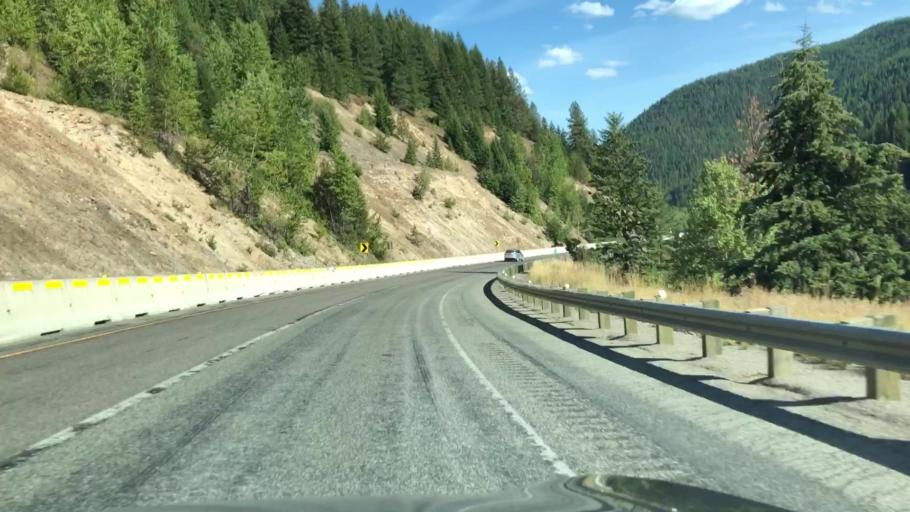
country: US
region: Montana
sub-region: Sanders County
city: Thompson Falls
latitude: 47.4012
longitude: -115.4637
